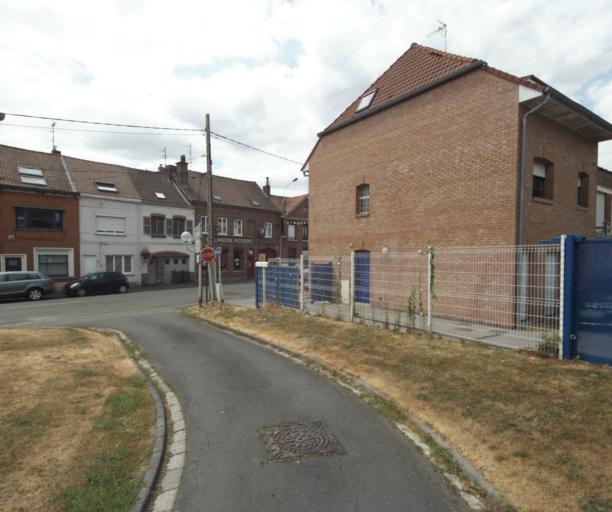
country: FR
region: Nord-Pas-de-Calais
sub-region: Departement du Nord
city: Mouvaux
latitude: 50.6965
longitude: 3.1431
